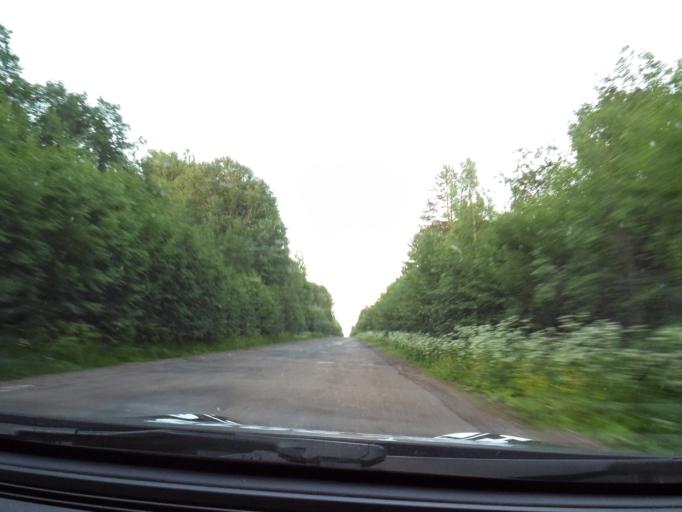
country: RU
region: Leningrad
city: Voznesen'ye
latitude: 60.8450
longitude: 35.6131
